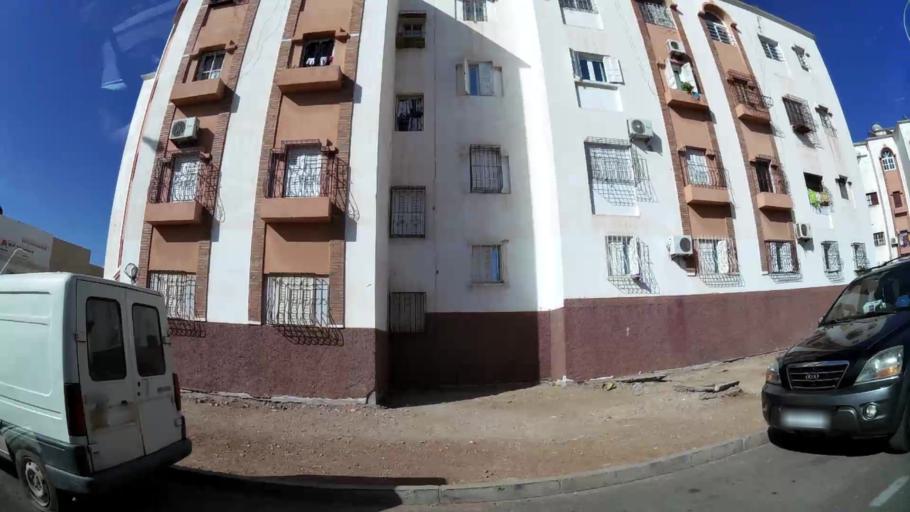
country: MA
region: Oued ed Dahab-Lagouira
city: Dakhla
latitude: 30.4181
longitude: -9.5677
